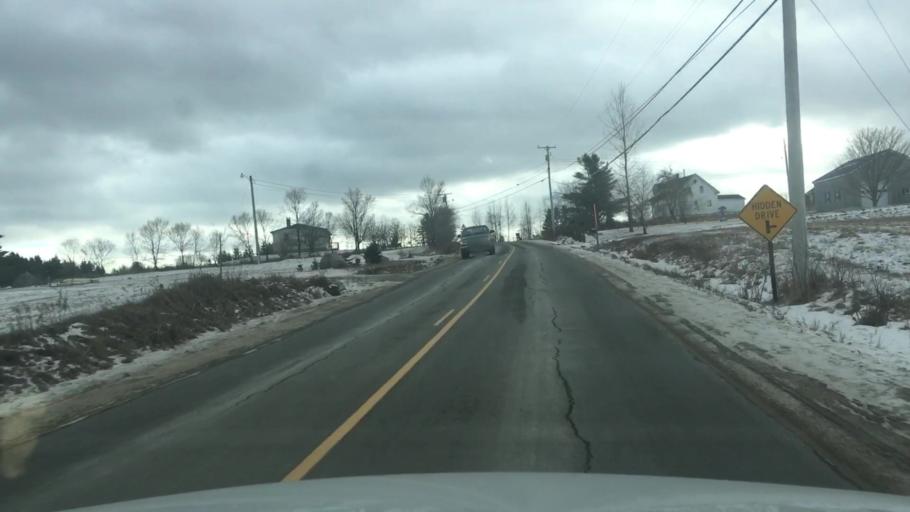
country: US
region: Maine
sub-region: Washington County
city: Machias
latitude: 44.6767
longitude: -67.4675
